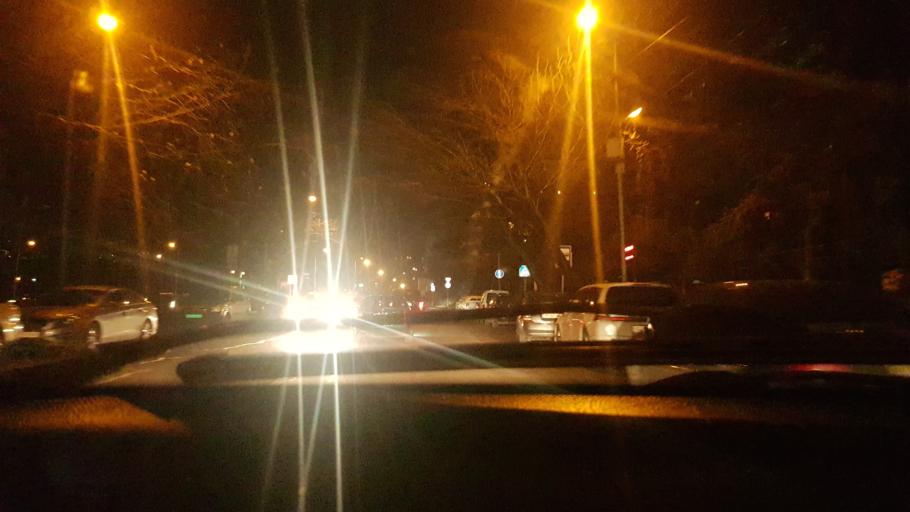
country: GE
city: Tsqnet'i
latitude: 41.7213
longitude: 44.7581
